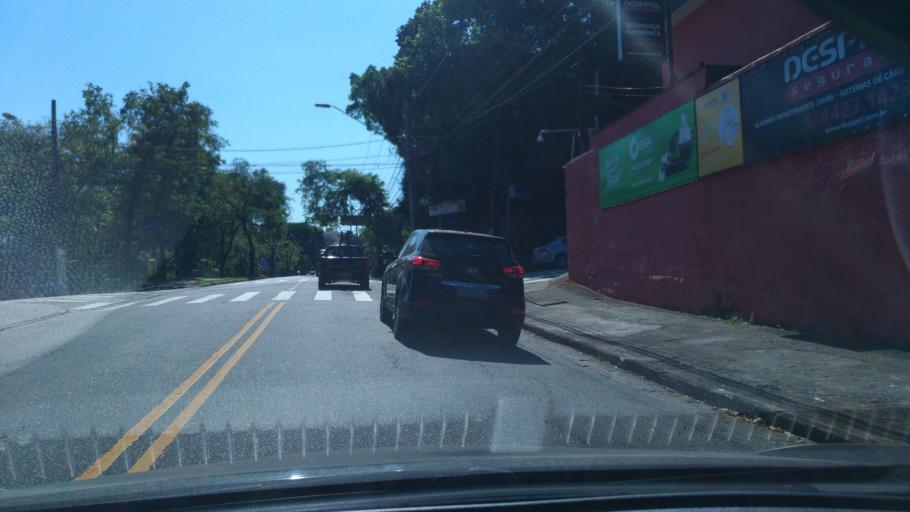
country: BR
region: Sao Paulo
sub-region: Santo Andre
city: Santo Andre
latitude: -23.6678
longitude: -46.5484
